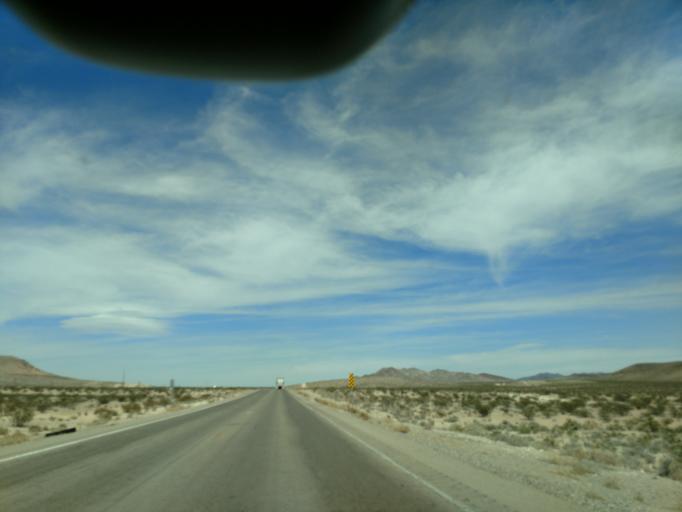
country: US
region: Nevada
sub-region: Clark County
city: Enterprise
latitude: 35.8566
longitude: -115.2543
